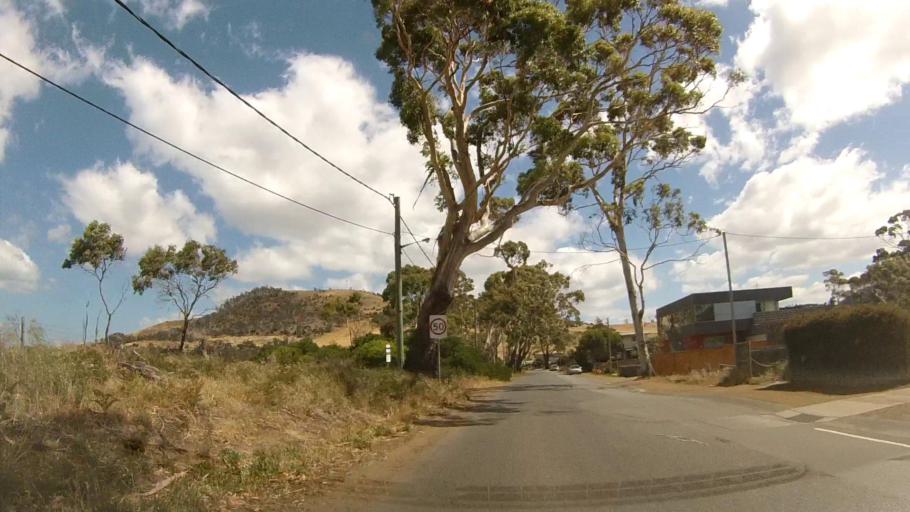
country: AU
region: Tasmania
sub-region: Clarence
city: Seven Mile Beach
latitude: -42.8620
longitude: 147.5053
